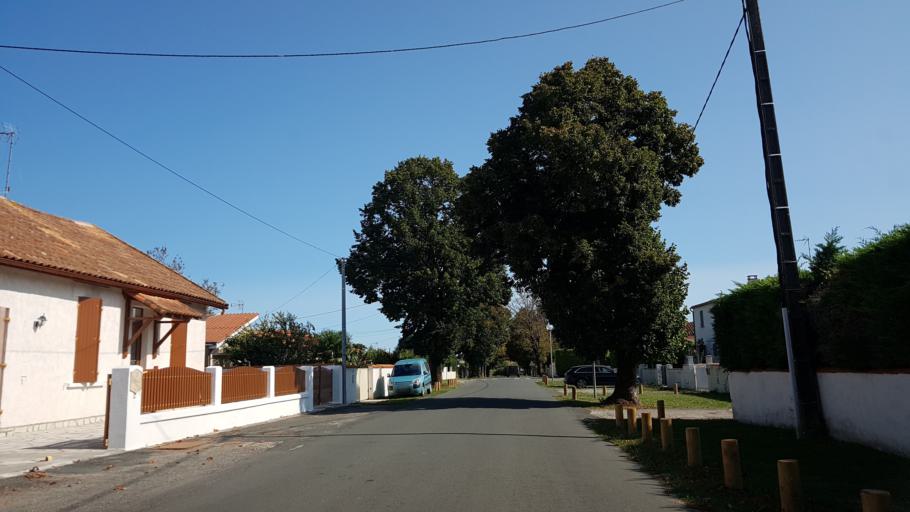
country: FR
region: Poitou-Charentes
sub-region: Departement de la Charente-Maritime
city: Breuillet
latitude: 45.7071
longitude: -1.0265
